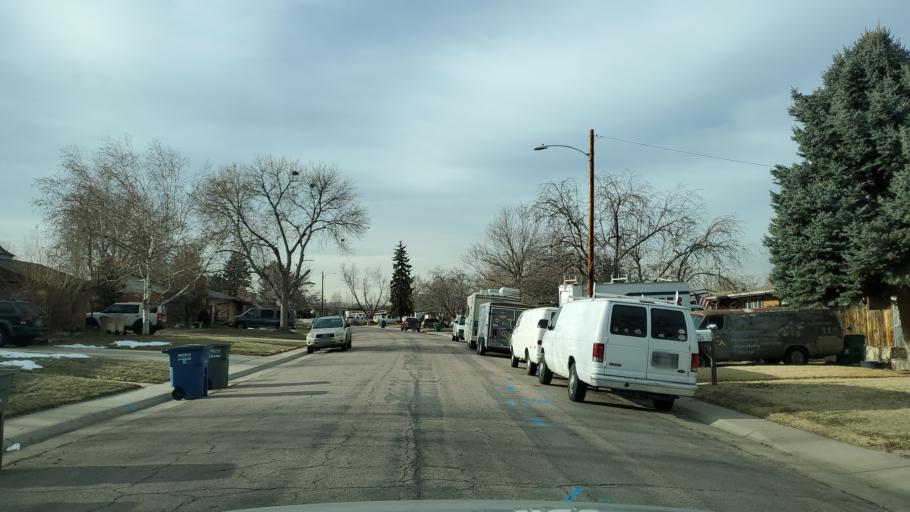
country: US
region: Colorado
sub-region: Adams County
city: Sherrelwood
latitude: 39.8366
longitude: -105.0184
